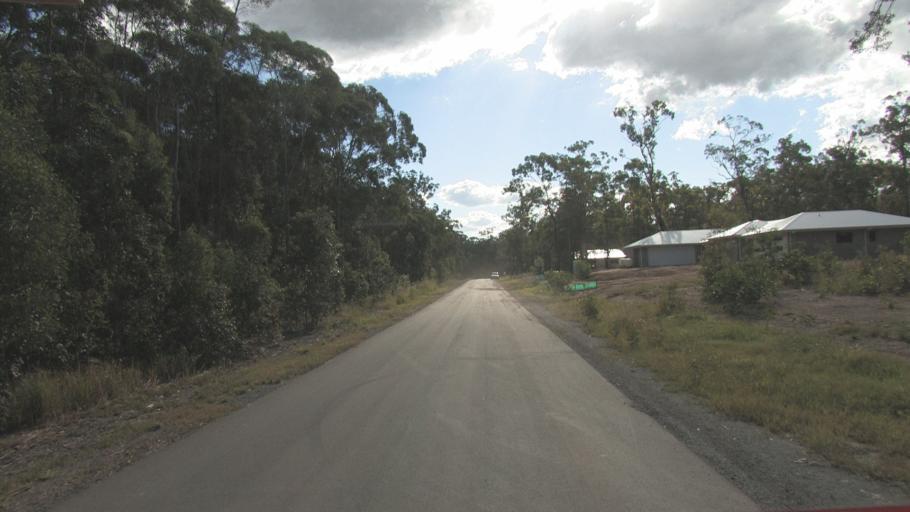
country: AU
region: Queensland
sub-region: Gold Coast
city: Yatala
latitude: -27.6678
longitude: 153.2527
